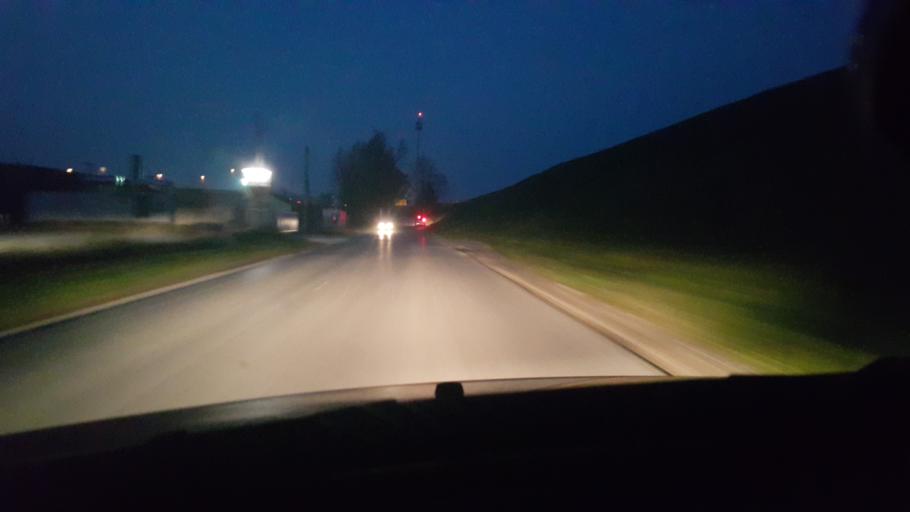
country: SI
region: Miklavz na Dravskem Polju
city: Miklavz na Dravskem Polju
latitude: 46.5235
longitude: 15.7013
